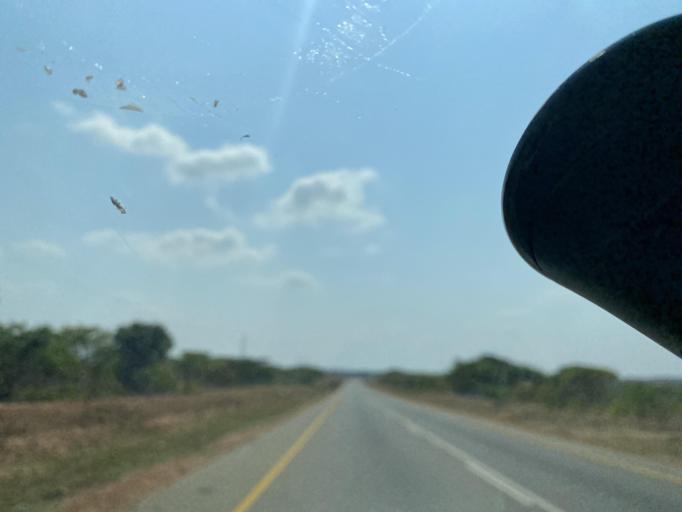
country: ZM
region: Lusaka
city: Chongwe
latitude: -15.5297
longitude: 28.6209
